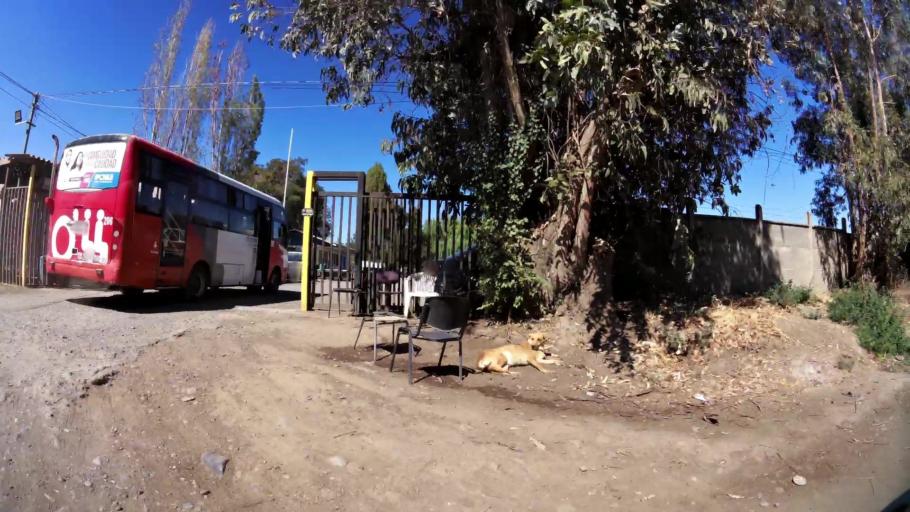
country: CL
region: O'Higgins
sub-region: Provincia de Cachapoal
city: Rancagua
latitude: -34.1704
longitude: -70.7000
